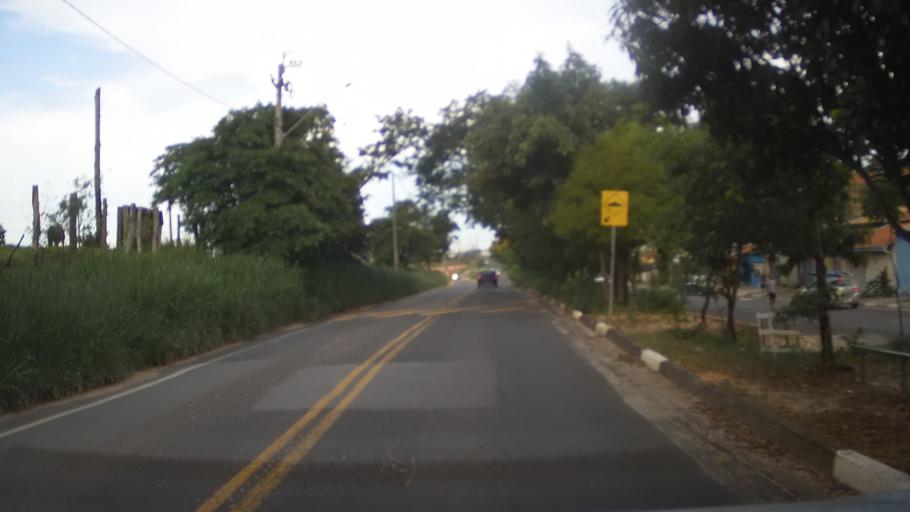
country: BR
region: Sao Paulo
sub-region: Hortolandia
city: Hortolandia
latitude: -22.9566
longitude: -47.2019
